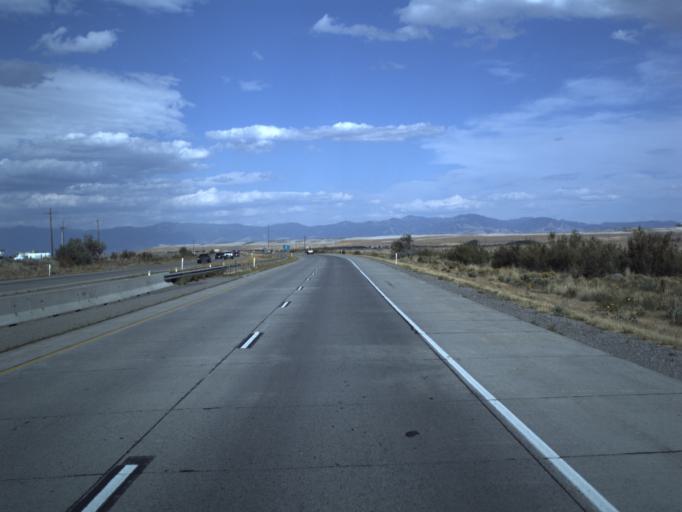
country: US
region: Utah
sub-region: Salt Lake County
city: Magna
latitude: 40.7293
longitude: -112.2100
